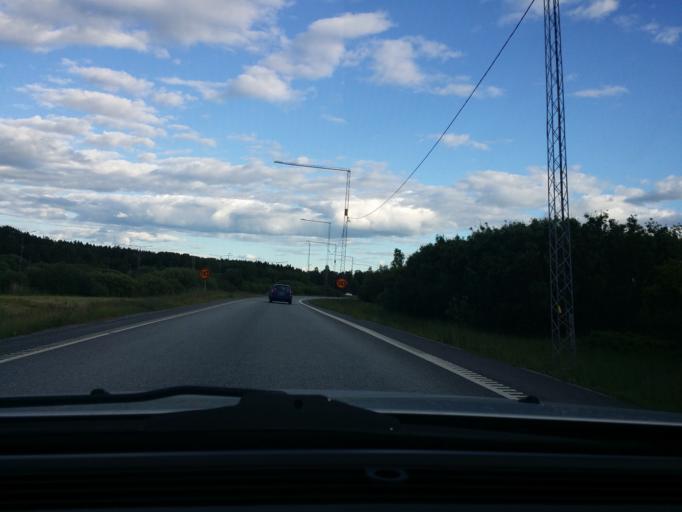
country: SE
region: Stockholm
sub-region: Sigtuna Kommun
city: Rosersberg
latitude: 59.6030
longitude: 17.8959
